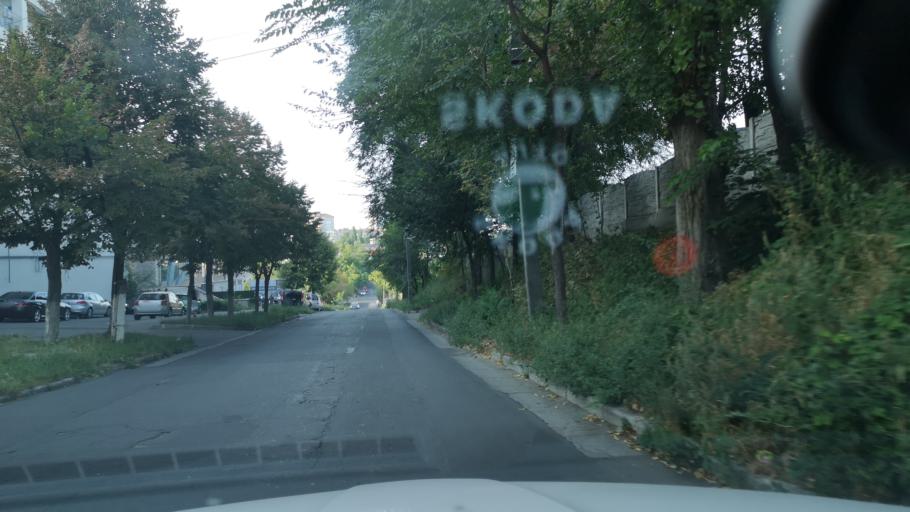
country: MD
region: Chisinau
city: Chisinau
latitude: 47.0083
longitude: 28.8489
